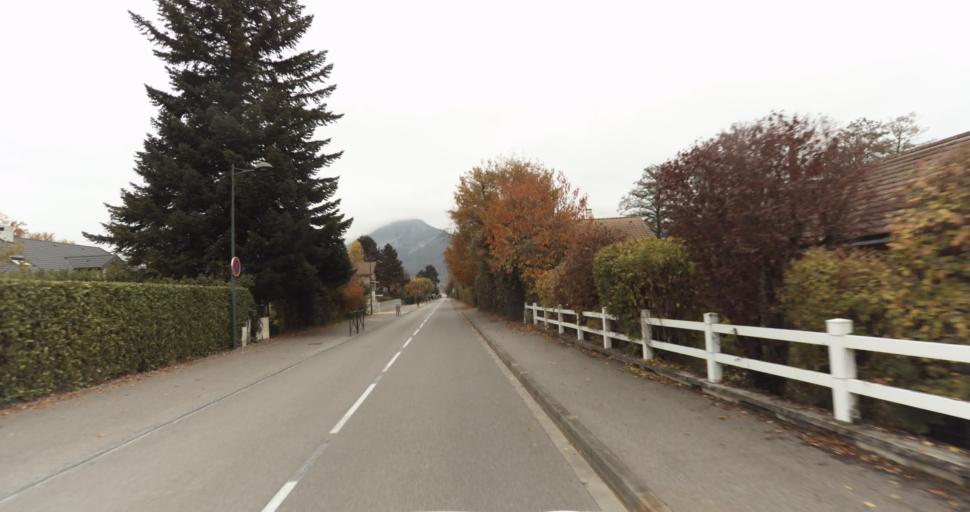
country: FR
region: Rhone-Alpes
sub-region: Departement de la Haute-Savoie
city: Saint-Jorioz
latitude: 45.8398
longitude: 6.1720
